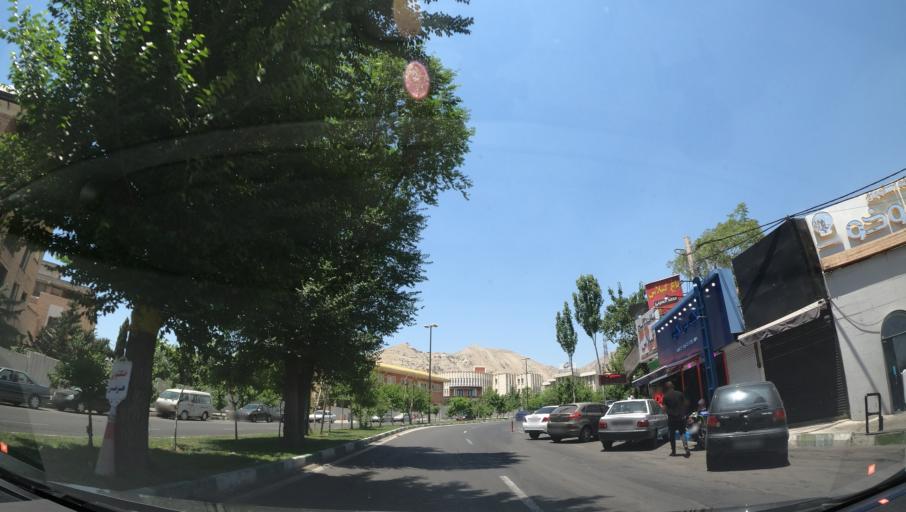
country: IR
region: Tehran
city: Tajrish
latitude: 35.8085
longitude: 51.3899
